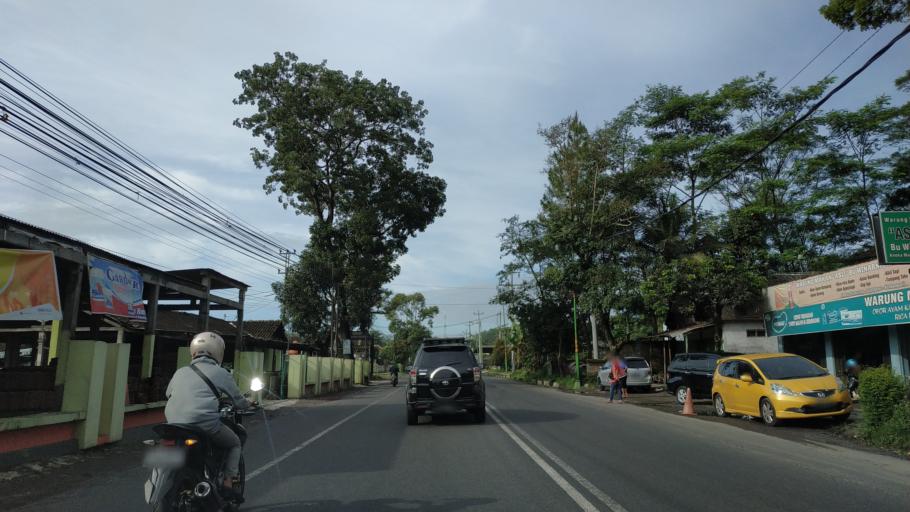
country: ID
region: Central Java
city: Salatiga
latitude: -7.3822
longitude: 110.5150
